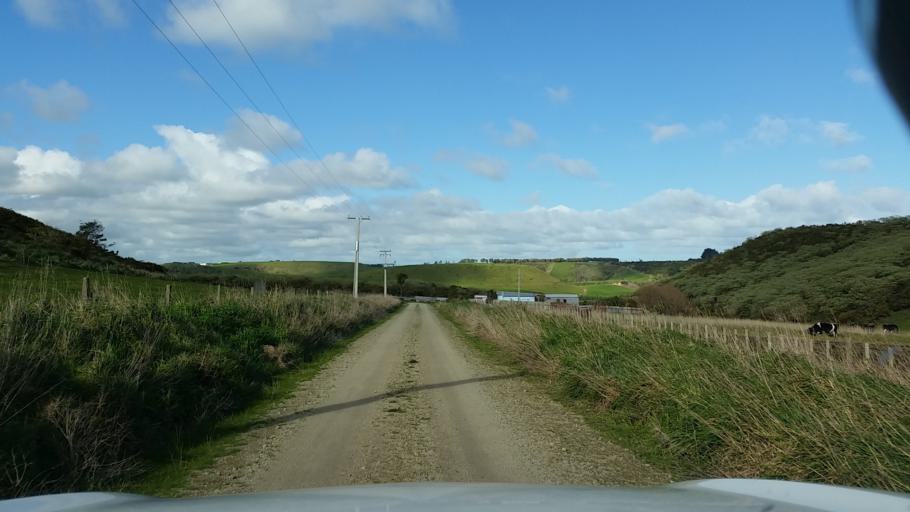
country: NZ
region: Taranaki
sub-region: South Taranaki District
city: Patea
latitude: -39.7198
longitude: 174.4702
